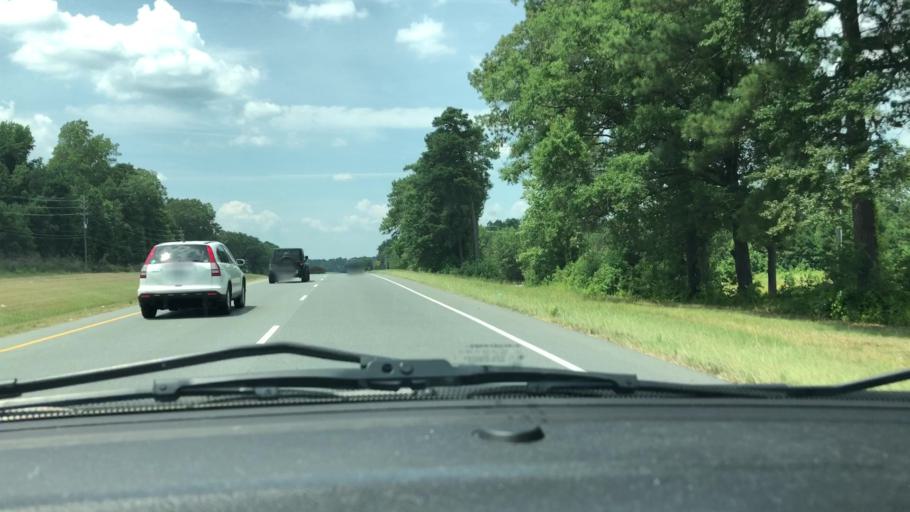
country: US
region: North Carolina
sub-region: Lee County
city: Sanford
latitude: 35.5057
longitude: -79.2080
